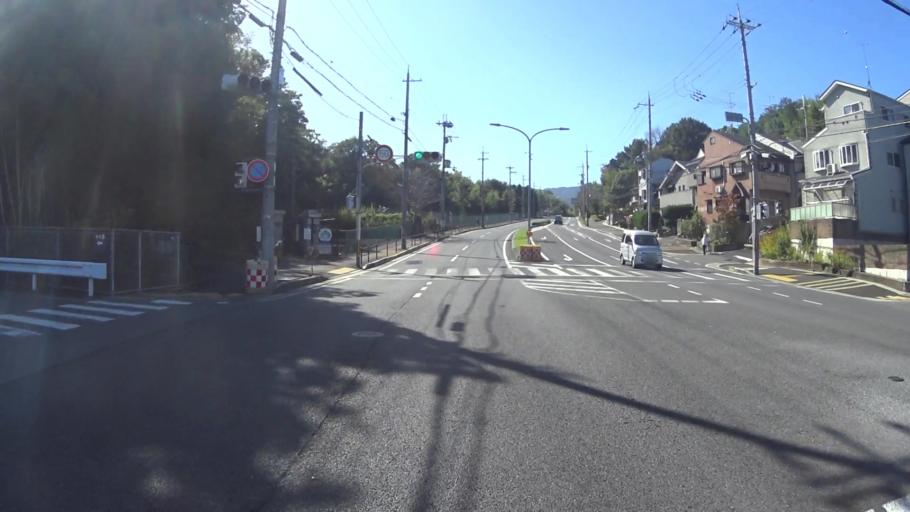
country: JP
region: Kyoto
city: Muko
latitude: 34.9640
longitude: 135.6867
